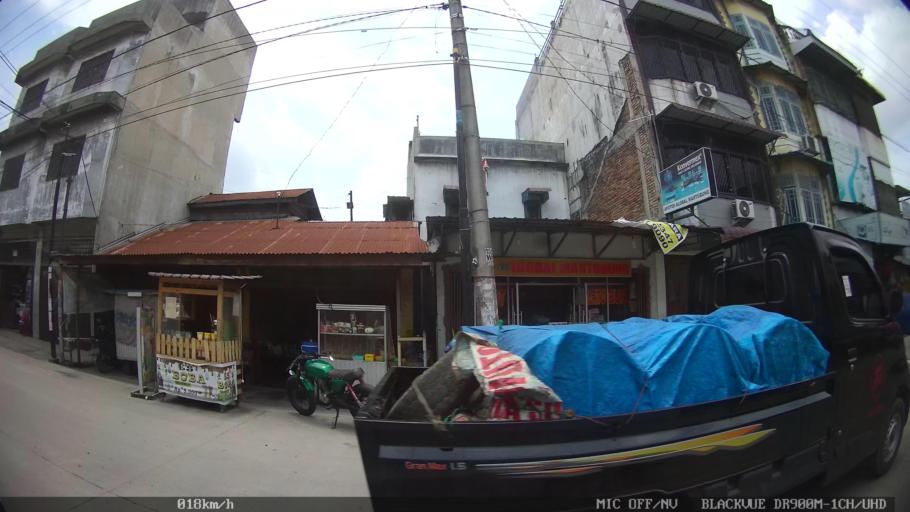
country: ID
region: North Sumatra
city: Labuhan Deli
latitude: 3.6963
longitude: 98.6735
